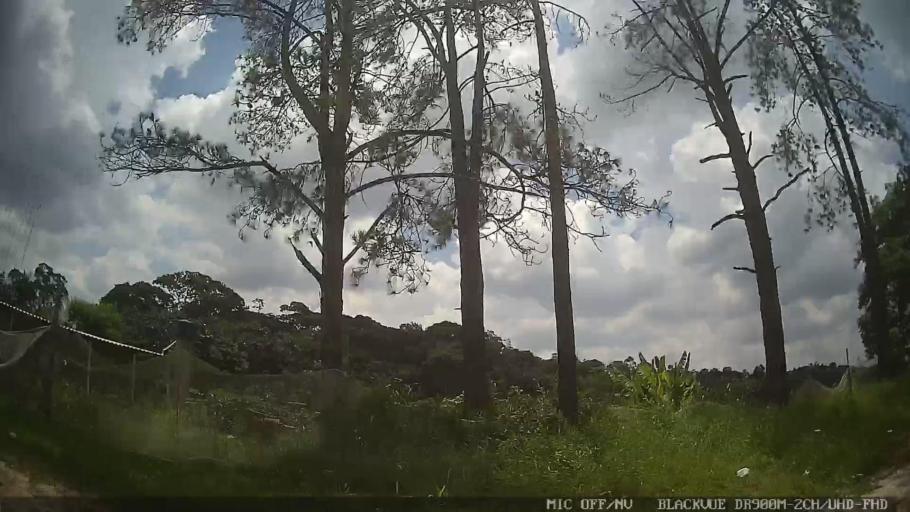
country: BR
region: Sao Paulo
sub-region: Ferraz De Vasconcelos
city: Ferraz de Vasconcelos
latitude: -23.6114
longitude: -46.3722
